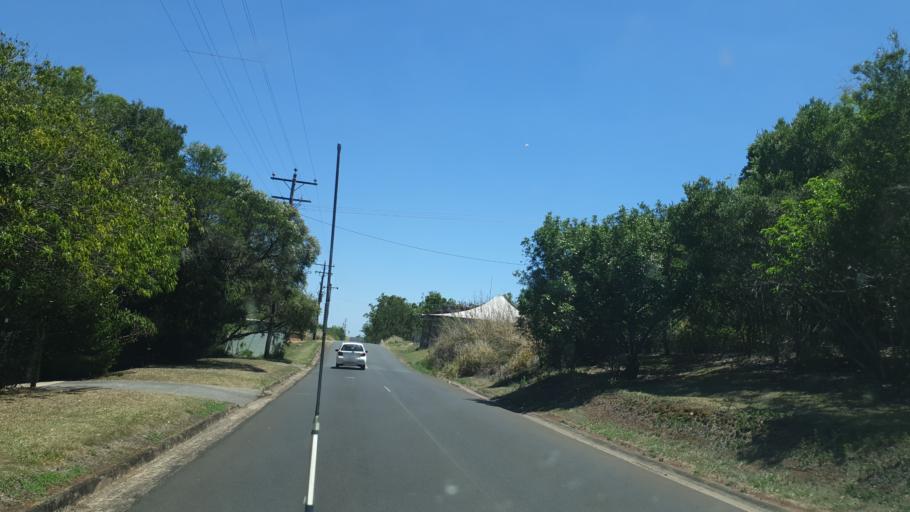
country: AU
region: Queensland
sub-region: Tablelands
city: Atherton
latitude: -17.2672
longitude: 145.4904
